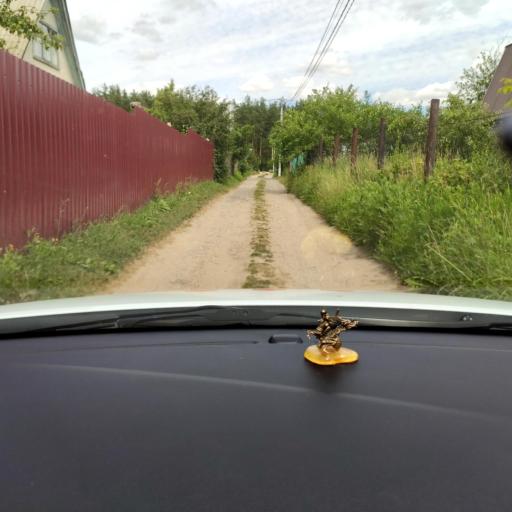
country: RU
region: Tatarstan
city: Staroye Arakchino
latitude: 55.8920
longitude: 49.0442
